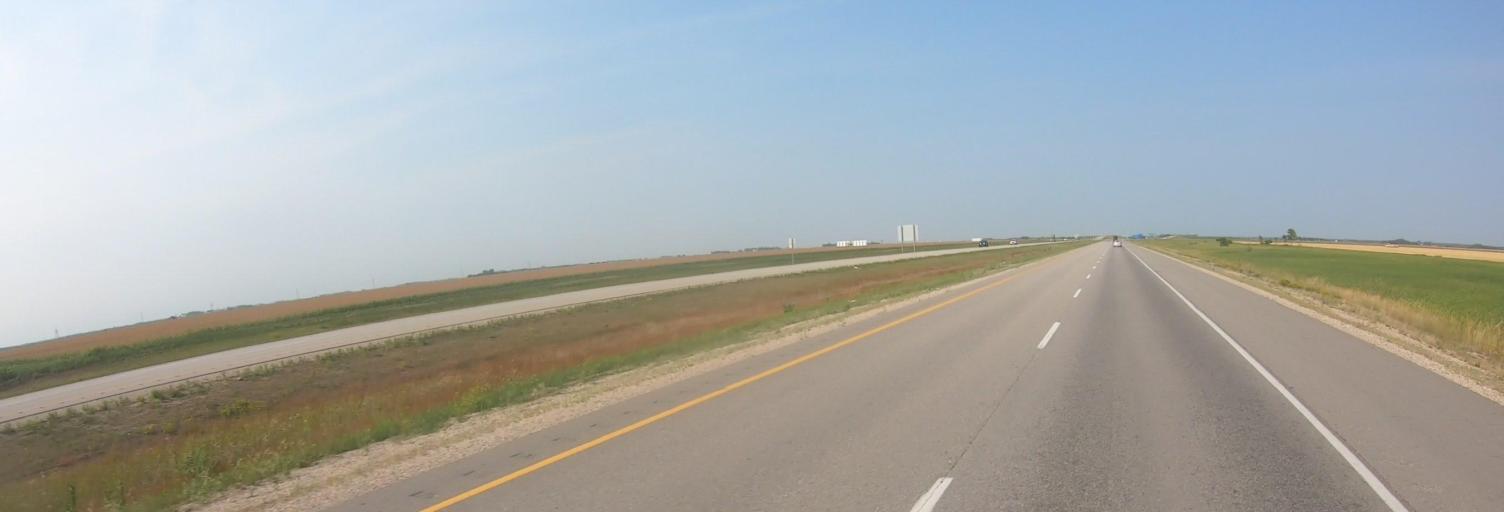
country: CA
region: Manitoba
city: Steinbach
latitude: 49.6858
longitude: -96.6569
